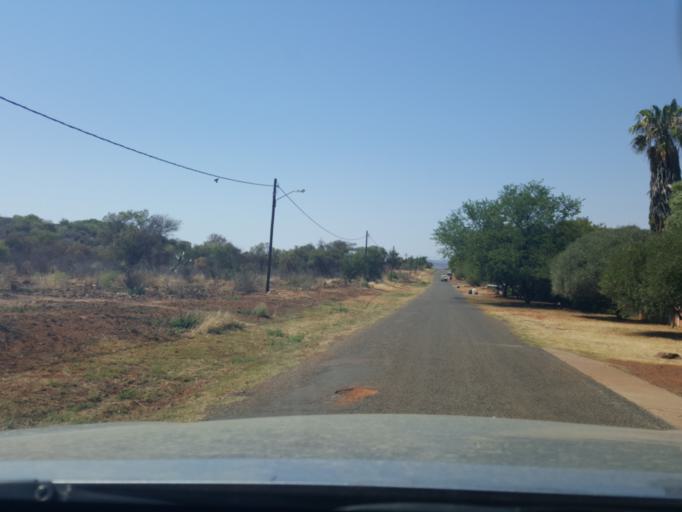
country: ZA
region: North-West
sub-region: Ngaka Modiri Molema District Municipality
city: Zeerust
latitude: -25.5274
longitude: 26.0804
